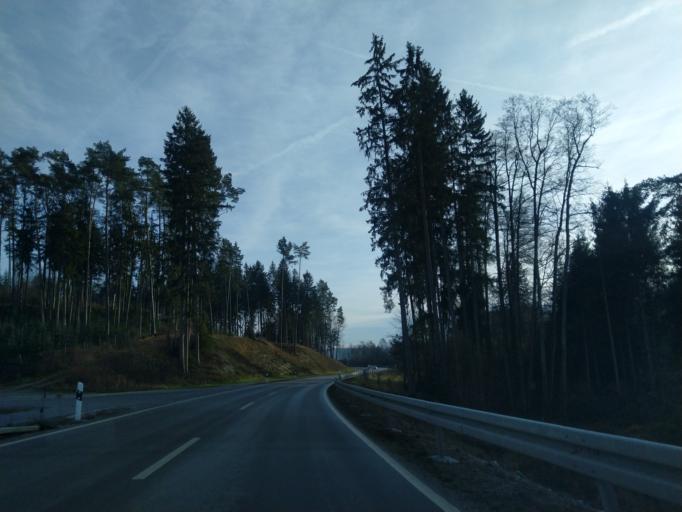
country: DE
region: Bavaria
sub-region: Lower Bavaria
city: Wallerfing
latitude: 48.6615
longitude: 12.8757
